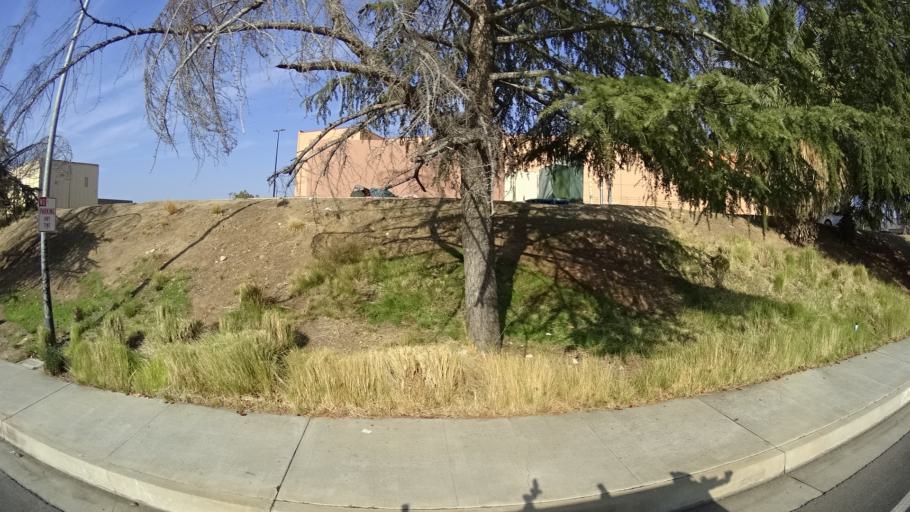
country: US
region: California
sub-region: Kern County
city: Bakersfield
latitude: 35.3917
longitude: -118.9586
